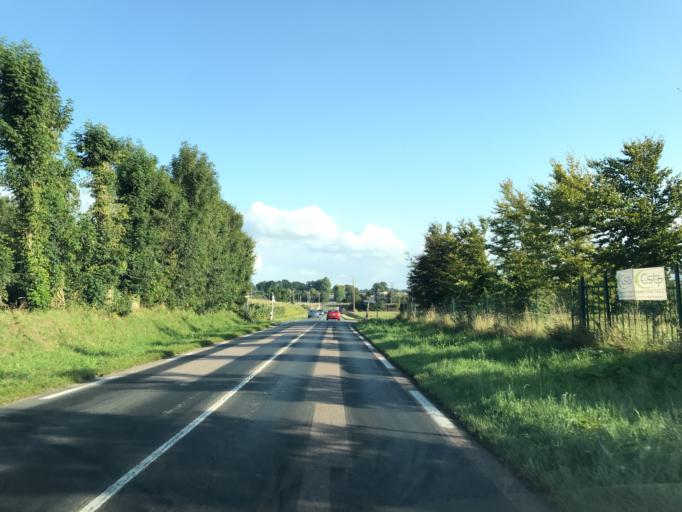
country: FR
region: Haute-Normandie
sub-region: Departement de la Seine-Maritime
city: Beuzeville-la-Grenier
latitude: 49.6061
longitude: 0.4141
